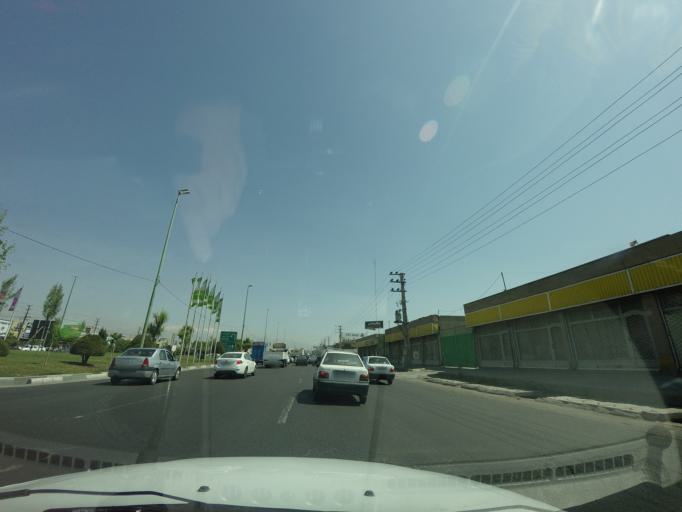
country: IR
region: Tehran
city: Eslamshahr
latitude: 35.5932
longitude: 51.2934
